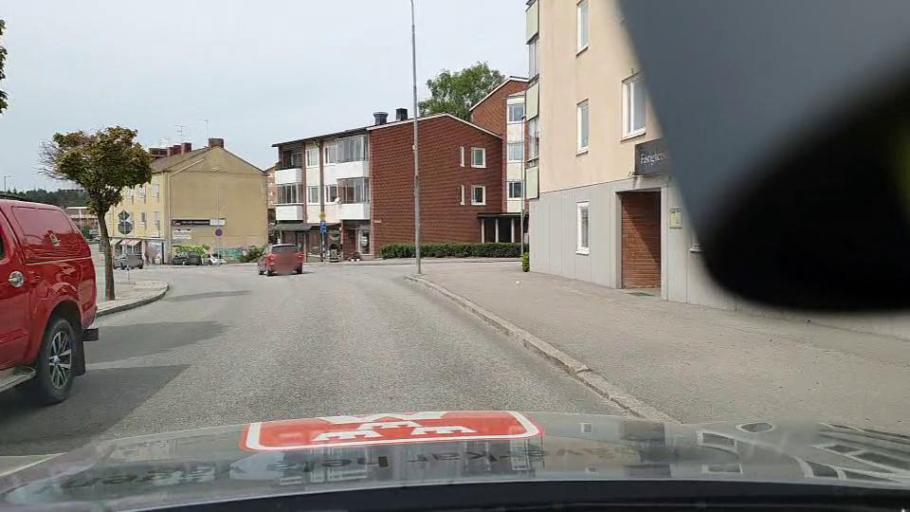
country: SE
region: Soedermanland
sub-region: Flens Kommun
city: Flen
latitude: 59.0573
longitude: 16.5942
